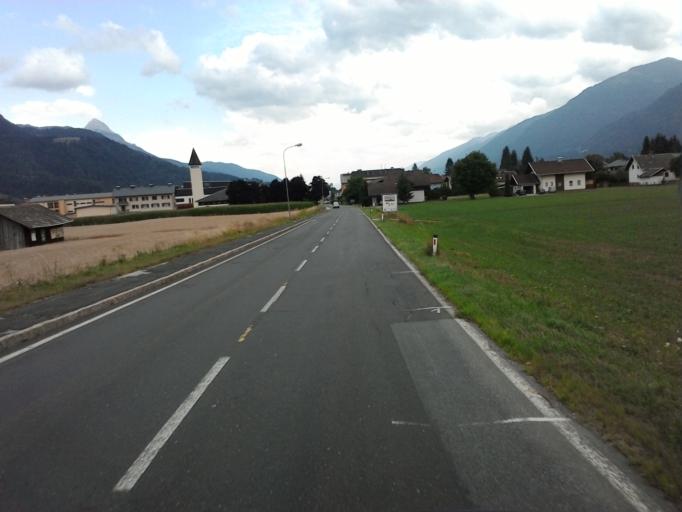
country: AT
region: Carinthia
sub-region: Politischer Bezirk Spittal an der Drau
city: Oberdrauburg
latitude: 46.6716
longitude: 12.9955
